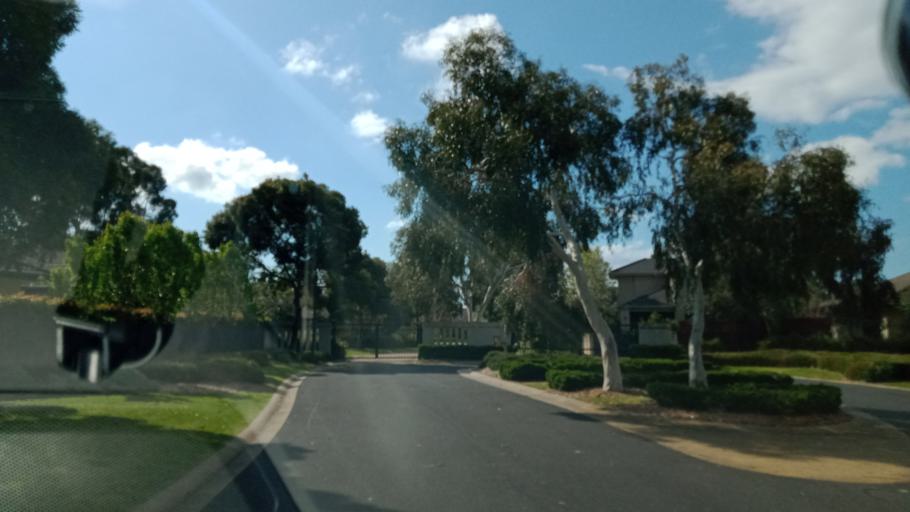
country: AU
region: Victoria
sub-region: Frankston
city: Sandhurst
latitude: -38.0800
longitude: 145.2072
